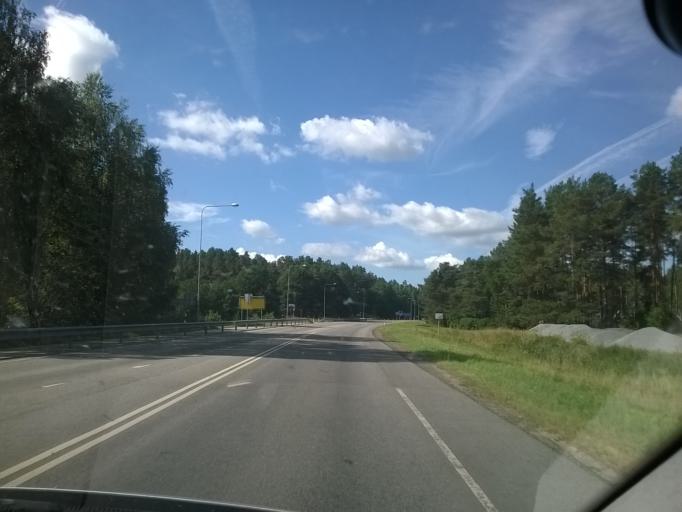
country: EE
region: Vorumaa
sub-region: Voru linn
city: Voru
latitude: 57.8198
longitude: 26.9986
